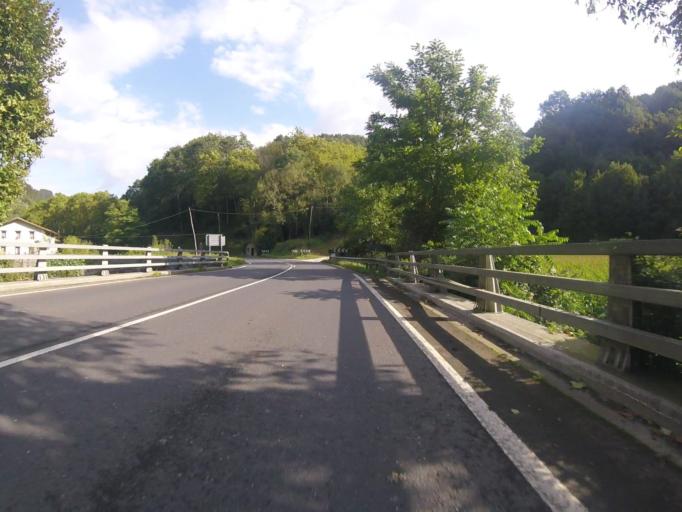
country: ES
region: Basque Country
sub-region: Provincia de Guipuzcoa
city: Orendain
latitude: 43.0751
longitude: -2.0869
